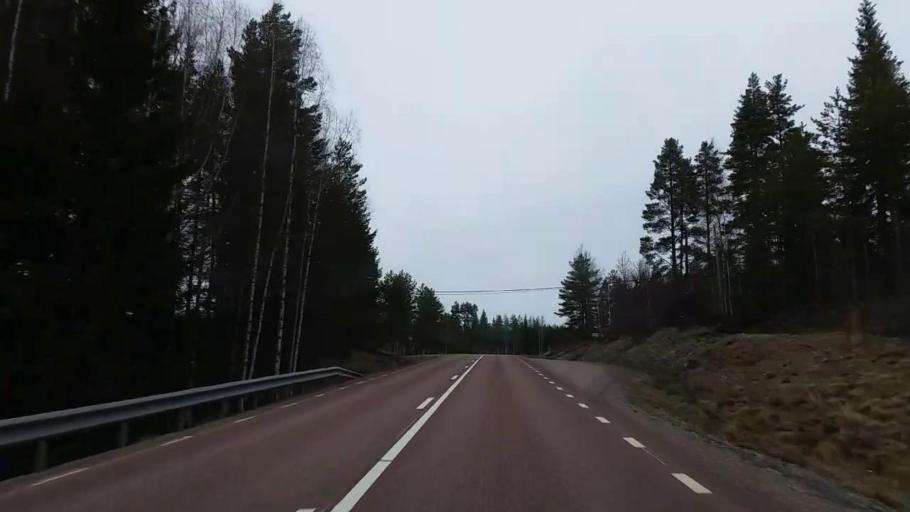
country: SE
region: Gaevleborg
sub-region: Ovanakers Kommun
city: Edsbyn
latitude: 61.2239
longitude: 15.8764
